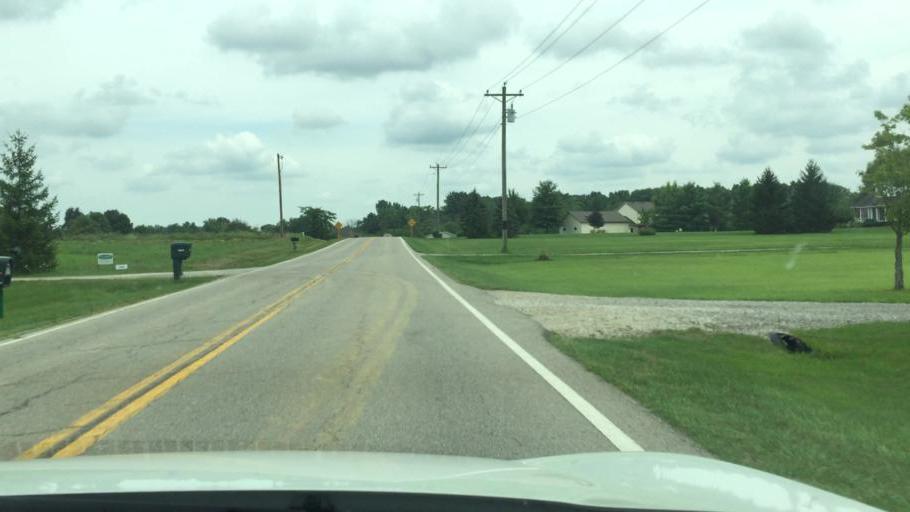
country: US
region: Ohio
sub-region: Union County
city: Marysville
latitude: 40.2266
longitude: -83.4591
